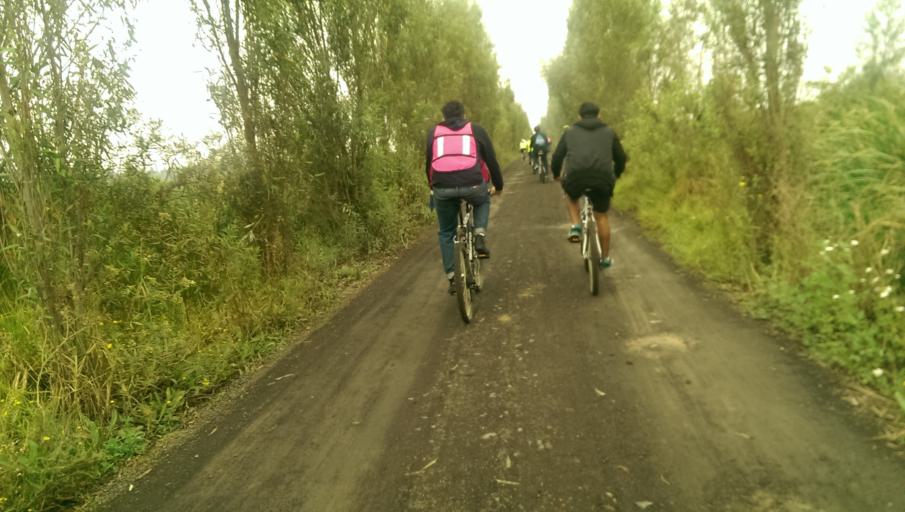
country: MX
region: Mexico City
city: Tlahuac
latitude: 19.2657
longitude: -99.0525
